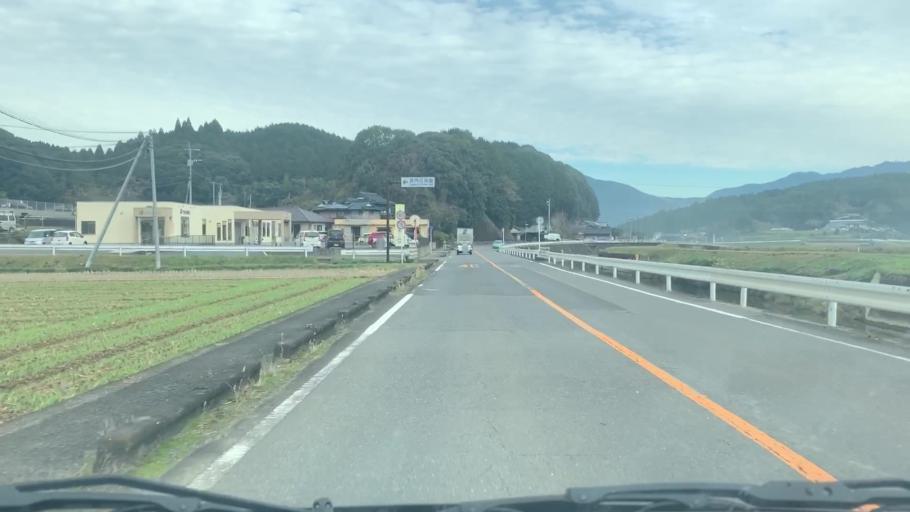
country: JP
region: Saga Prefecture
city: Takeocho-takeo
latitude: 33.2292
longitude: 129.9640
